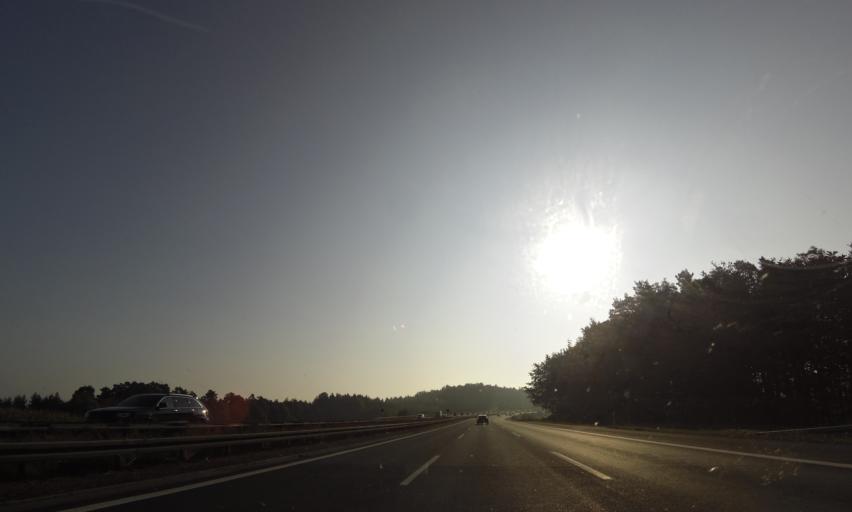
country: DE
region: Bavaria
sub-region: Upper Franconia
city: Pegnitz
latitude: 49.7904
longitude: 11.5024
